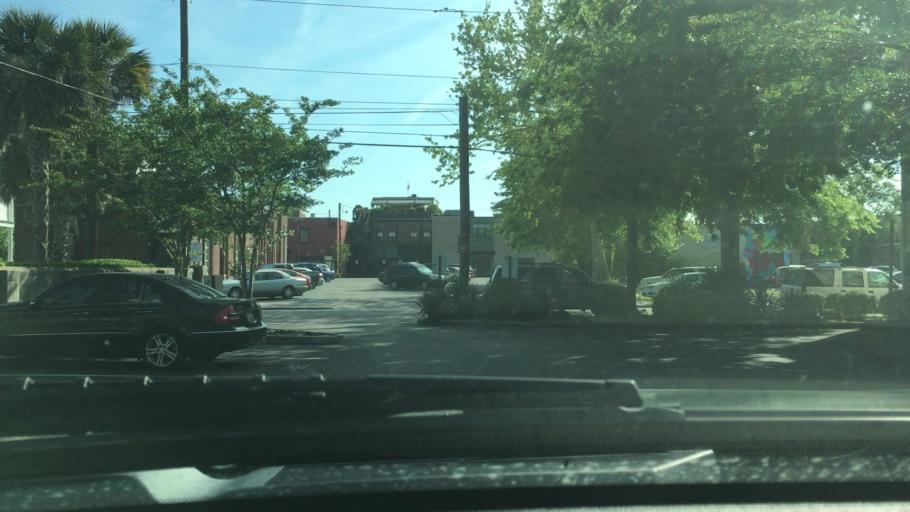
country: US
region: South Carolina
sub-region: Charleston County
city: Charleston
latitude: 32.7892
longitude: -79.9408
